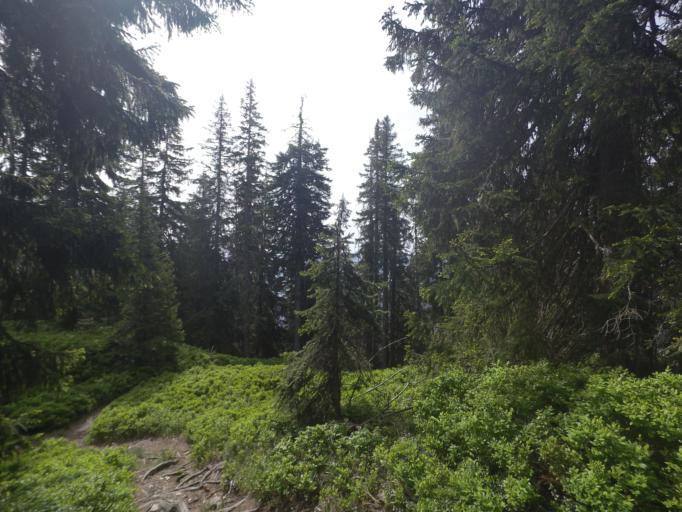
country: AT
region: Salzburg
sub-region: Politischer Bezirk Sankt Johann im Pongau
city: Muhlbach am Hochkonig
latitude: 47.3688
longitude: 13.0838
